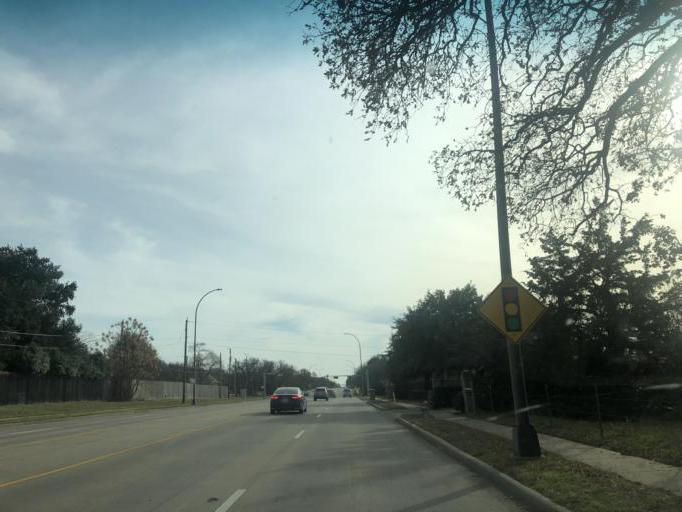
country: US
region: Texas
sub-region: Tarrant County
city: Dalworthington Gardens
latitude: 32.6937
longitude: -97.1494
